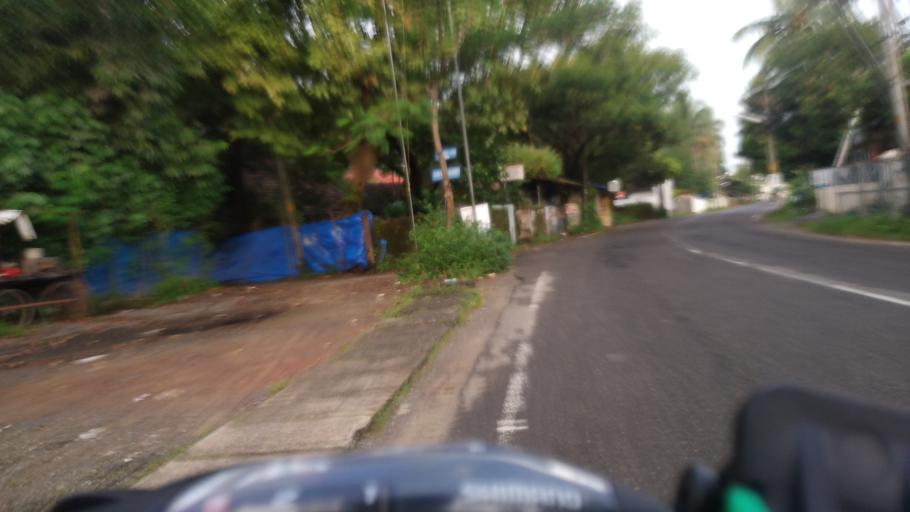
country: IN
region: Kerala
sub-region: Ernakulam
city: Cochin
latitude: 9.9747
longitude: 76.2429
